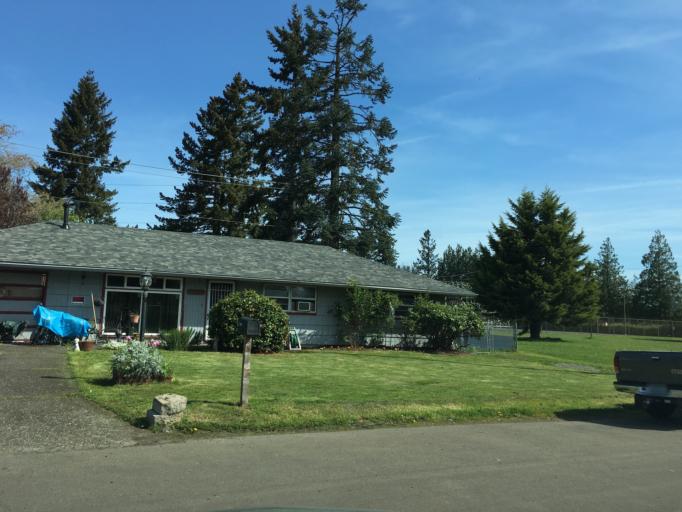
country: US
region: Oregon
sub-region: Multnomah County
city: Lents
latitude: 45.5321
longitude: -122.5301
